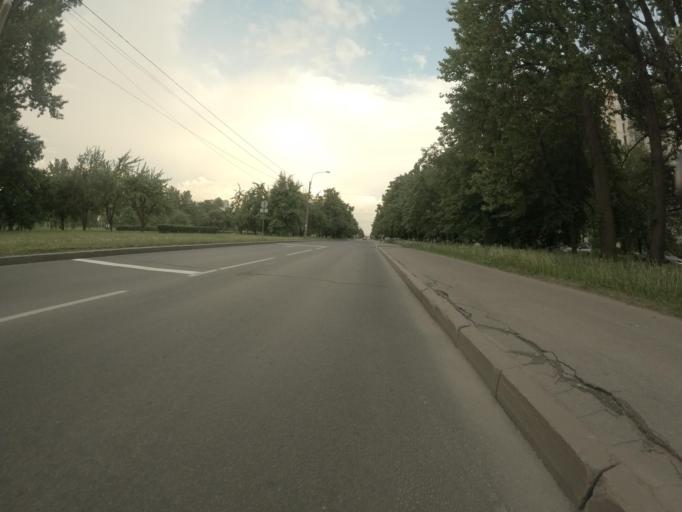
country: RU
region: St.-Petersburg
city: Kupchino
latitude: 59.8373
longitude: 30.3196
